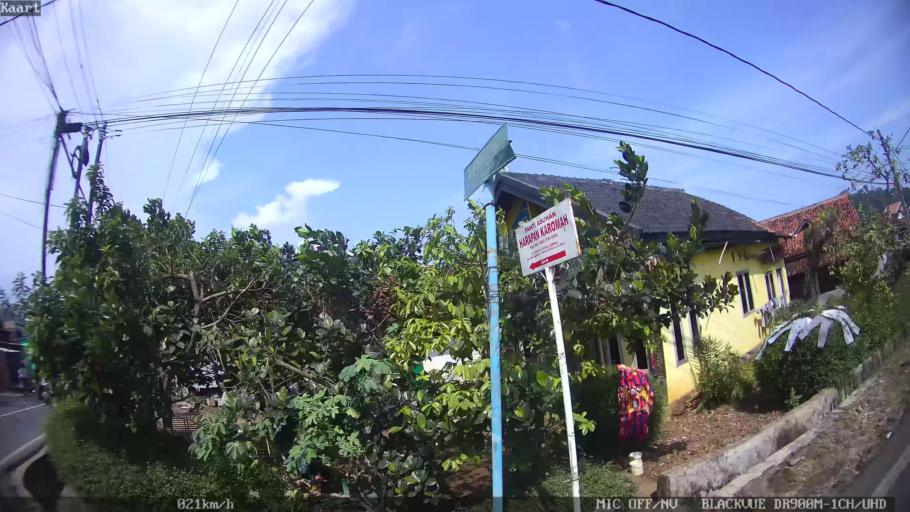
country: ID
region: Lampung
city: Kedaton
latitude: -5.3915
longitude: 105.2377
